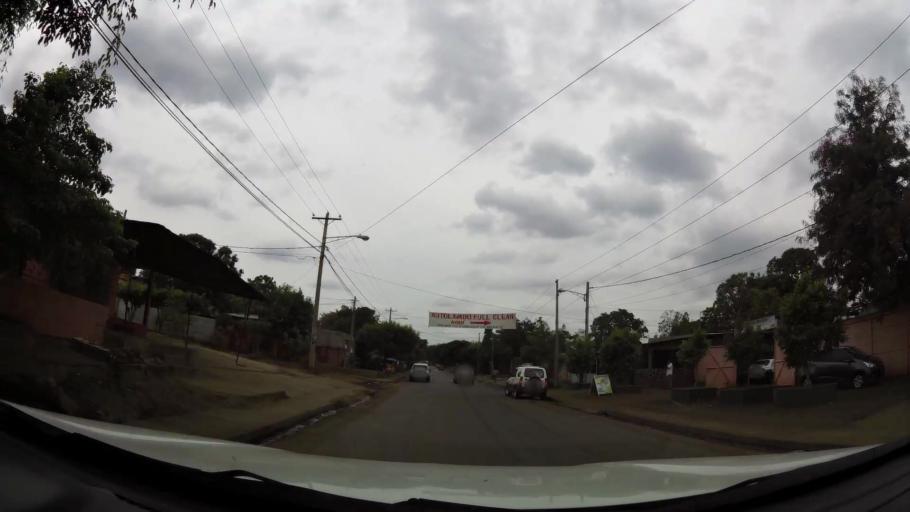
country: NI
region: Managua
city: Managua
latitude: 12.1220
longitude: -86.1952
